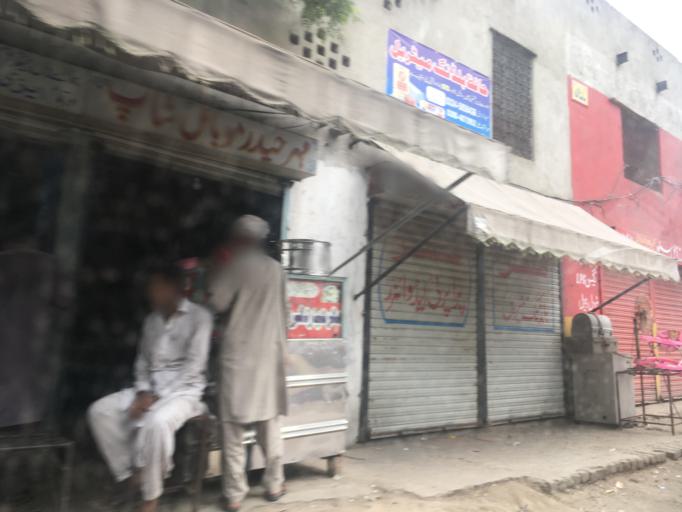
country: PK
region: Punjab
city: Lahore
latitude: 31.6161
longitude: 74.3675
